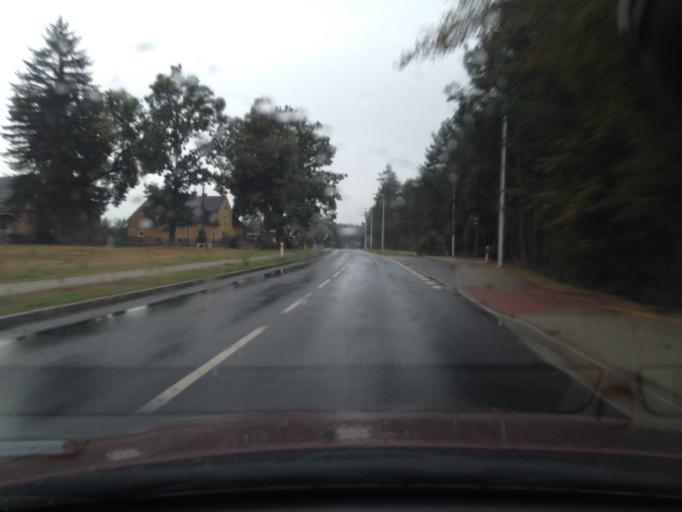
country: PL
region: Lubusz
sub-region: Powiat zaganski
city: Ilowa
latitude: 51.4685
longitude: 15.1995
